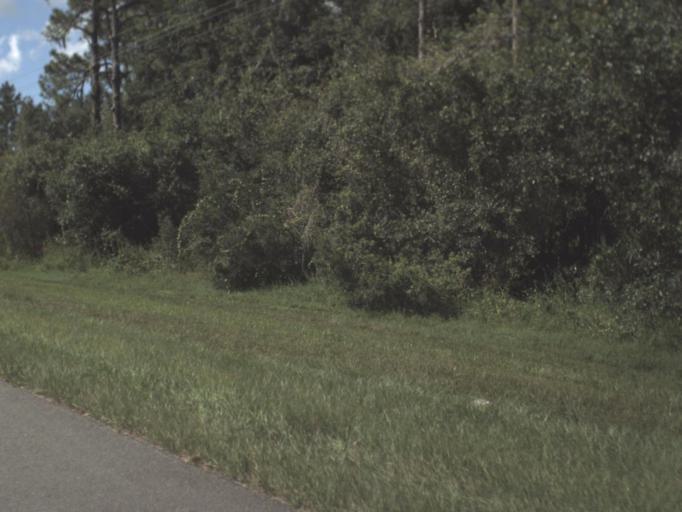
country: US
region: Florida
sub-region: Sarasota County
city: The Meadows
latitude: 27.4095
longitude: -82.3339
